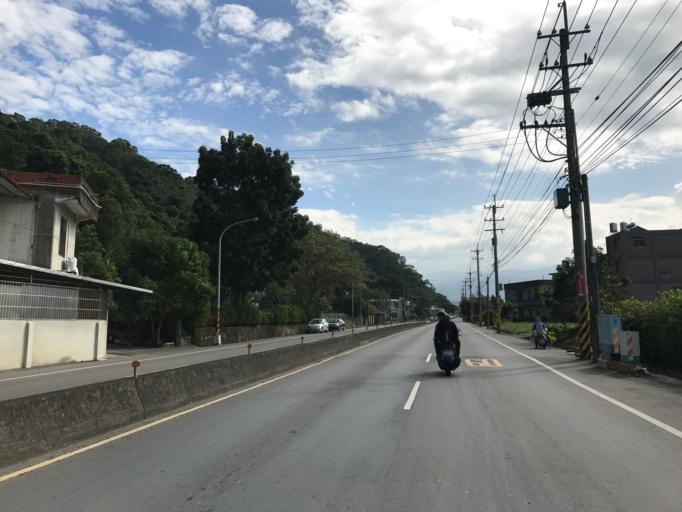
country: TW
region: Taiwan
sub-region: Hsinchu
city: Zhubei
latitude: 24.7423
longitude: 121.1075
